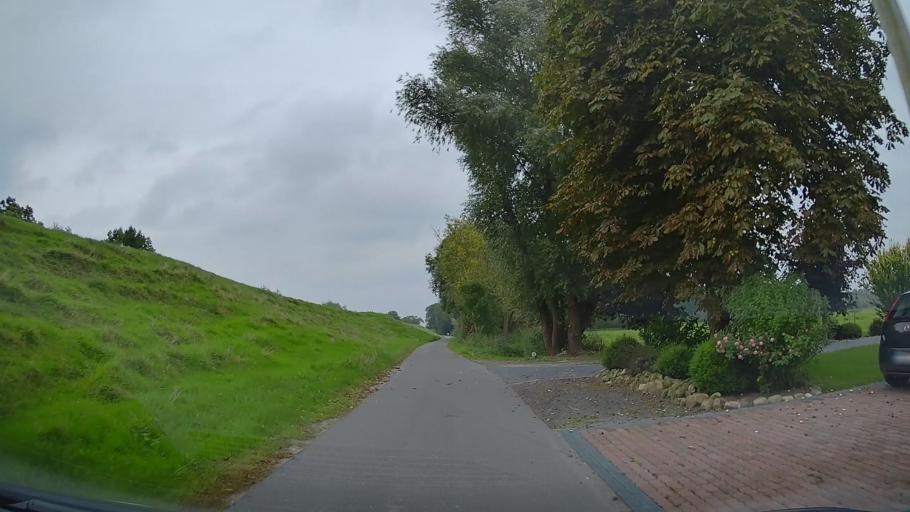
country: DE
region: Lower Saxony
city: Oederquart
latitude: 53.8292
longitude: 9.2543
